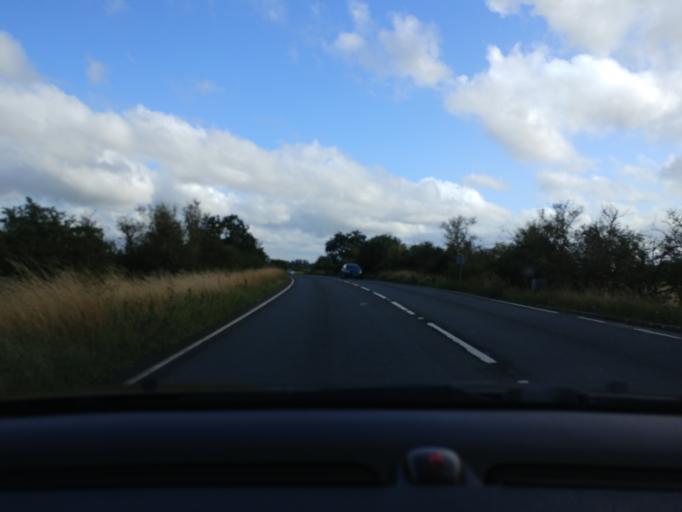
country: GB
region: England
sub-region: Oxfordshire
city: Bicester
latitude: 51.8771
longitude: -1.2305
